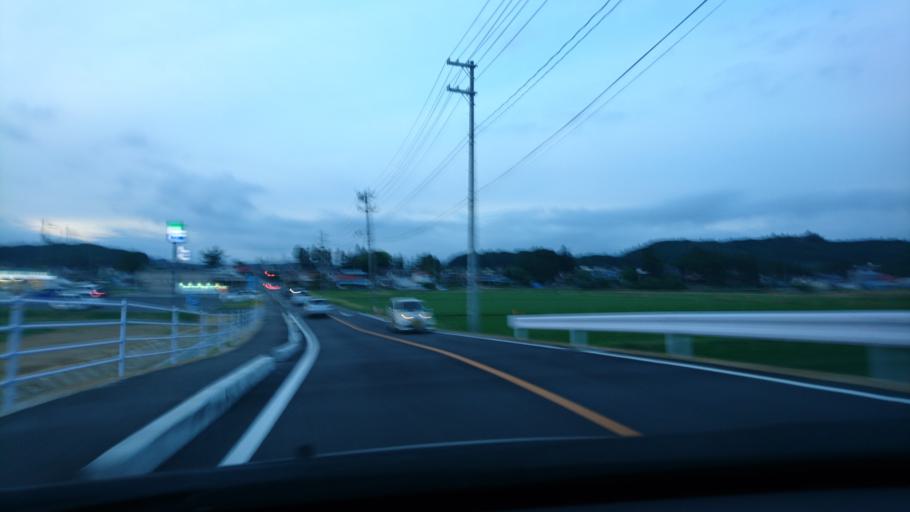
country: JP
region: Iwate
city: Ichinoseki
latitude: 38.8069
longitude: 140.9835
